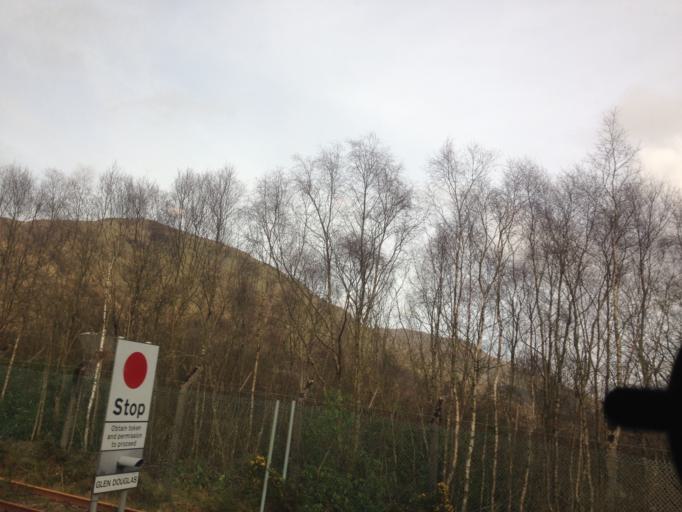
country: GB
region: Scotland
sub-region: Argyll and Bute
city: Garelochhead
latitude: 56.1576
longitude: -4.7792
